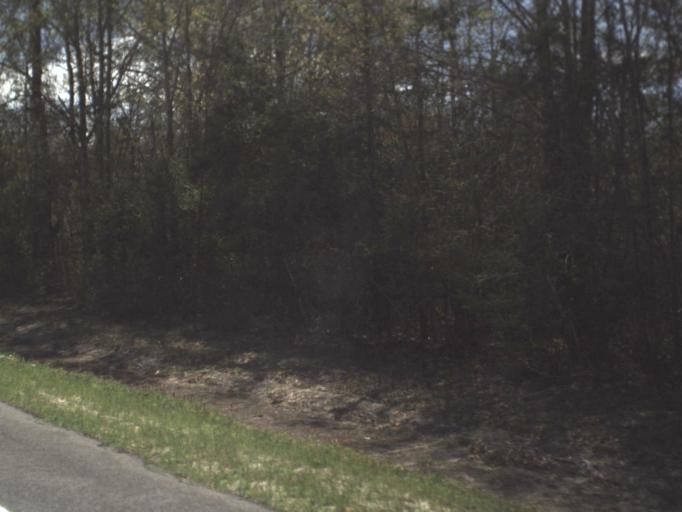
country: US
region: Alabama
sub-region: Geneva County
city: Geneva
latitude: 30.9283
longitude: -85.9649
